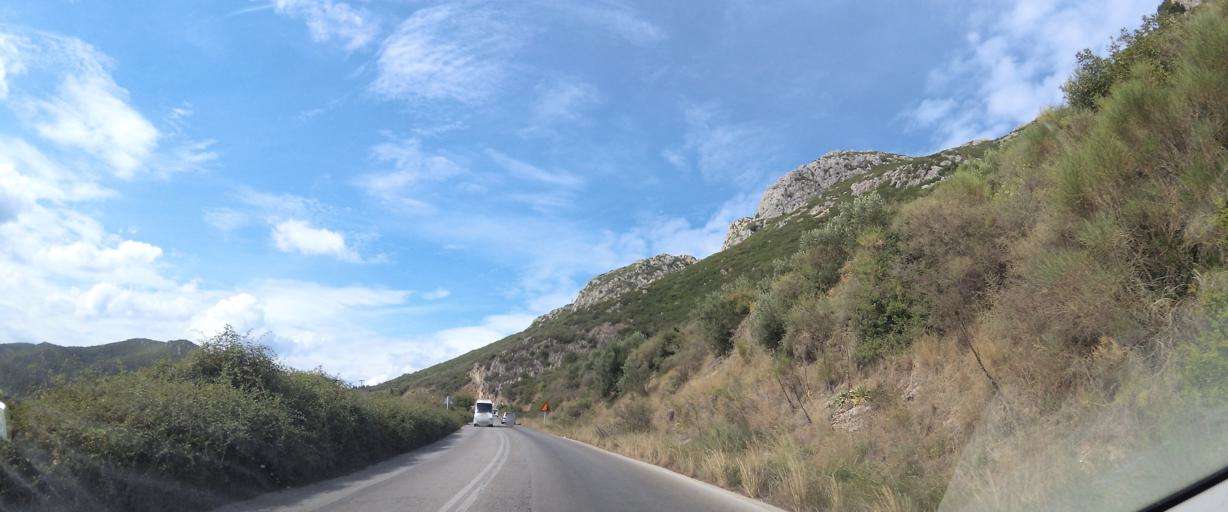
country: GR
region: Ionian Islands
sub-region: Nomos Kerkyras
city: Agios Georgis
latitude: 39.7045
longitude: 19.7609
